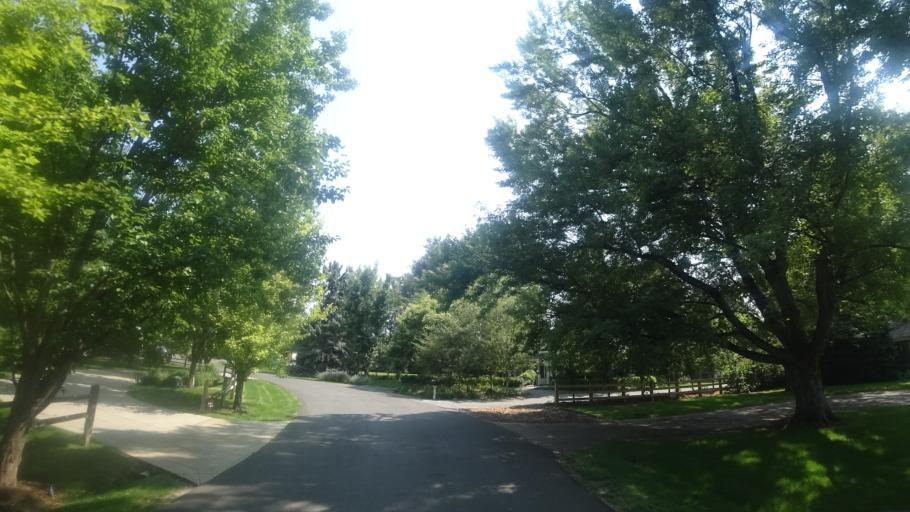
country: US
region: Colorado
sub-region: Arapahoe County
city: Cherry Hills Village
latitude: 39.6258
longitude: -104.9775
